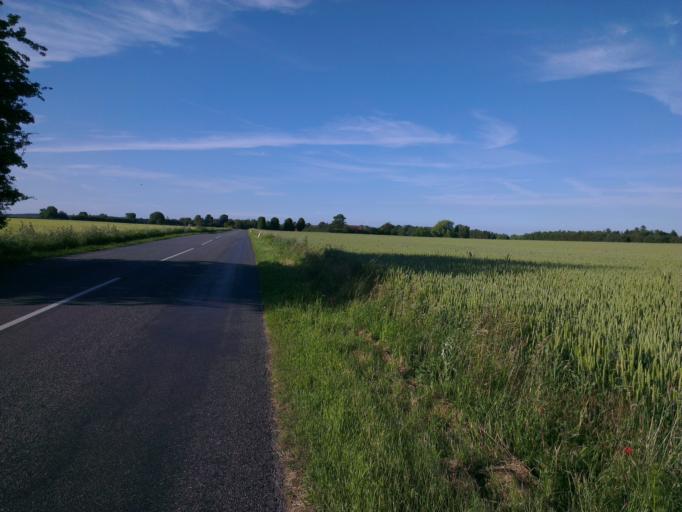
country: DK
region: Capital Region
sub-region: Frederikssund Kommune
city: Frederikssund
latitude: 55.8020
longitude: 12.0211
